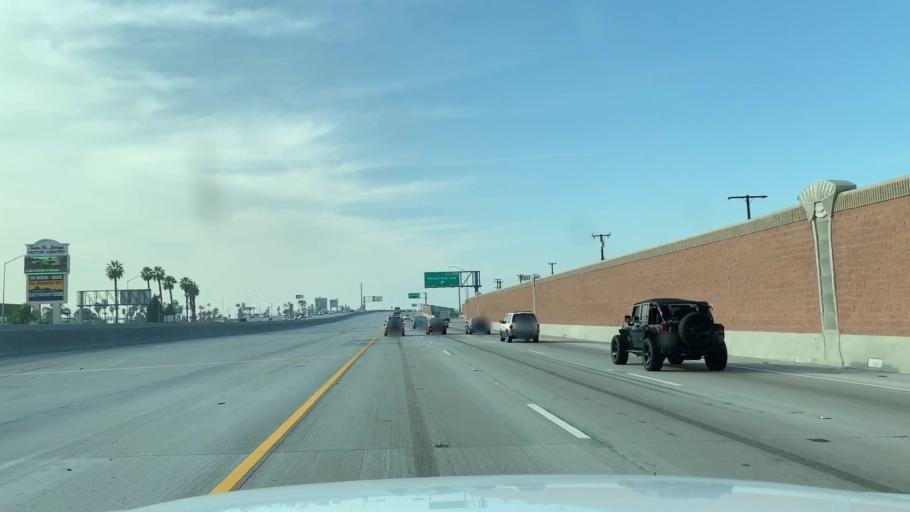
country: US
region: California
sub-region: Los Angeles County
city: Norwalk
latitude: 33.8993
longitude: -118.0563
